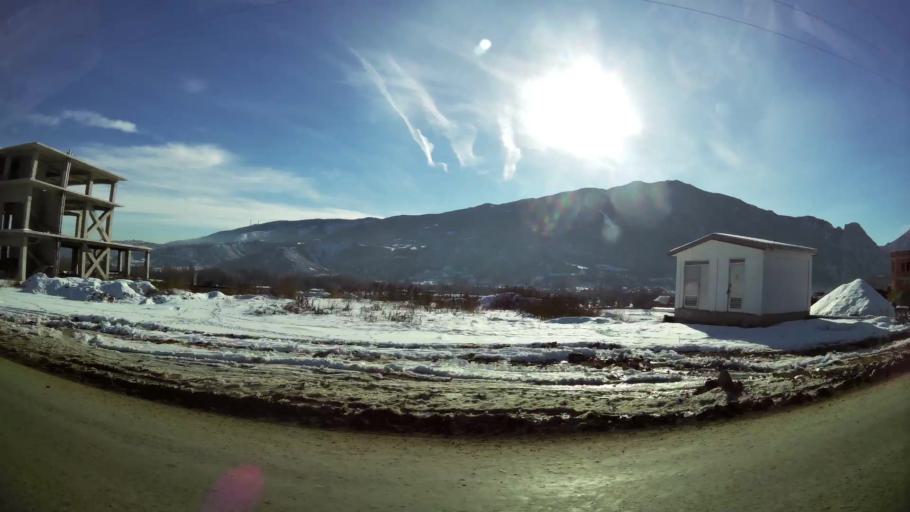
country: MK
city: Ljubin
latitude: 41.9863
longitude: 21.3072
